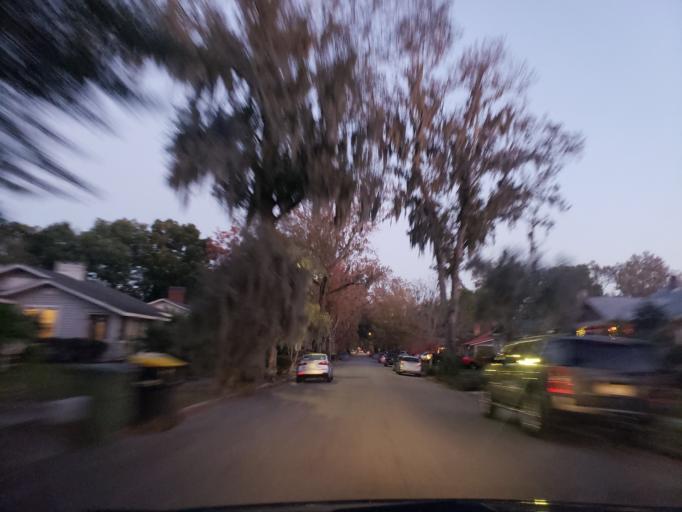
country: US
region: Georgia
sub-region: Chatham County
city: Thunderbolt
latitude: 32.0438
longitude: -81.0847
